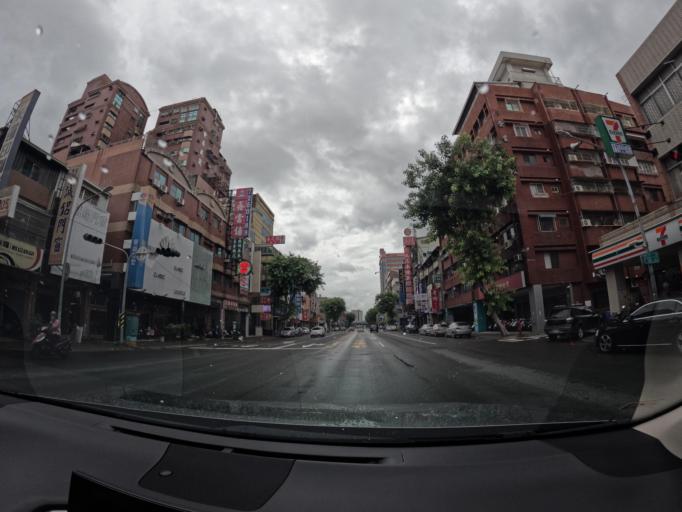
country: TW
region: Kaohsiung
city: Kaohsiung
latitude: 22.6319
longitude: 120.3319
